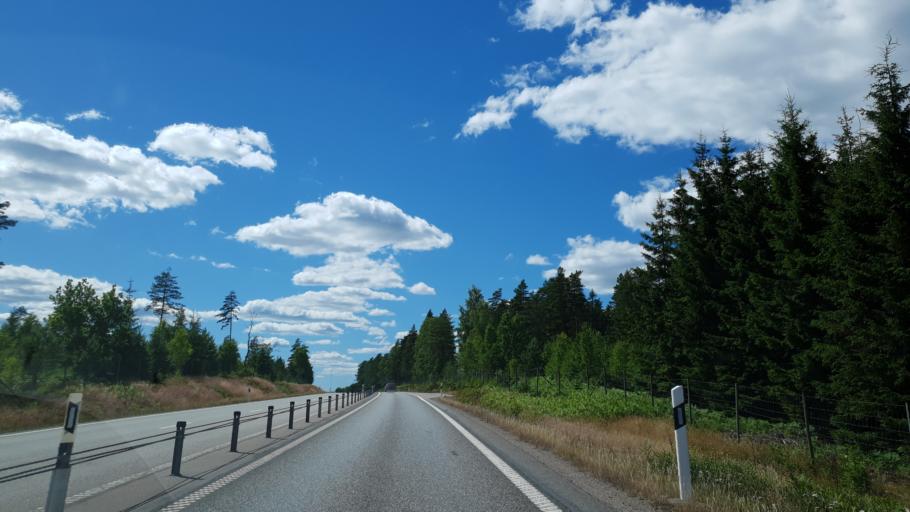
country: SE
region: Kronoberg
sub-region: Vaxjo Kommun
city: Ingelstad
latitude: 56.8701
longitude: 14.9884
